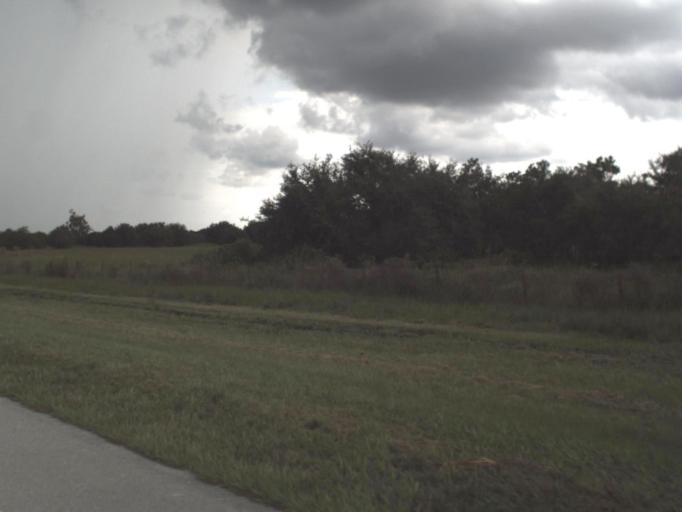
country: US
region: Florida
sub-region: Hendry County
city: Port LaBelle
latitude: 26.9147
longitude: -81.3245
